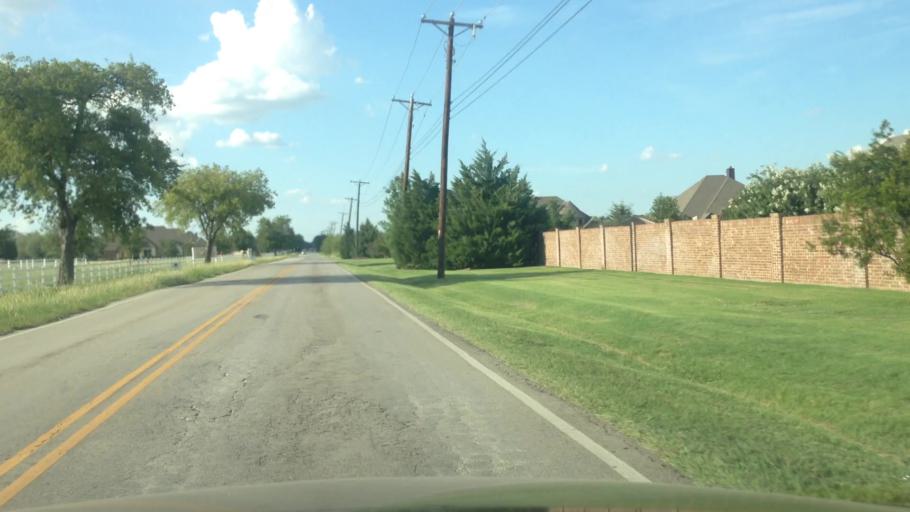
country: US
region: Texas
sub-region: Tarrant County
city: Haslet
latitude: 32.9628
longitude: -97.3919
